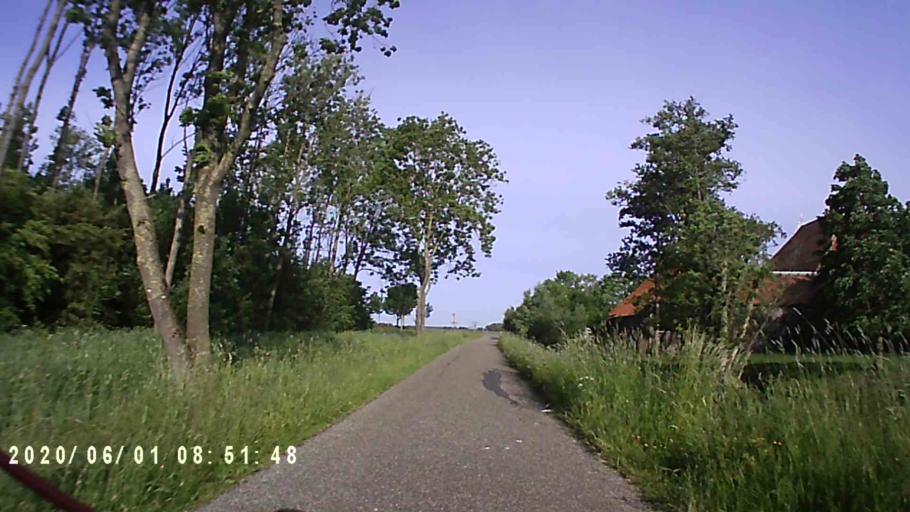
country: NL
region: Friesland
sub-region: Gemeente Ferwerderadiel
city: Burdaard
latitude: 53.2759
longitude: 5.8359
